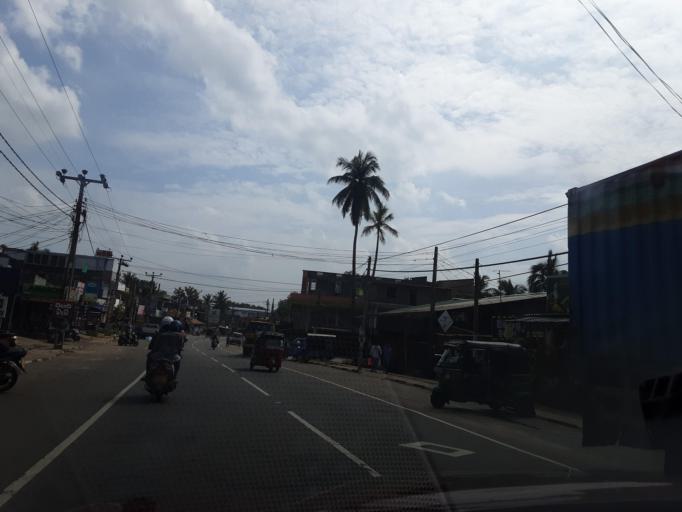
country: LK
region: Northern Province
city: Vavuniya
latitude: 8.5378
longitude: 80.4936
